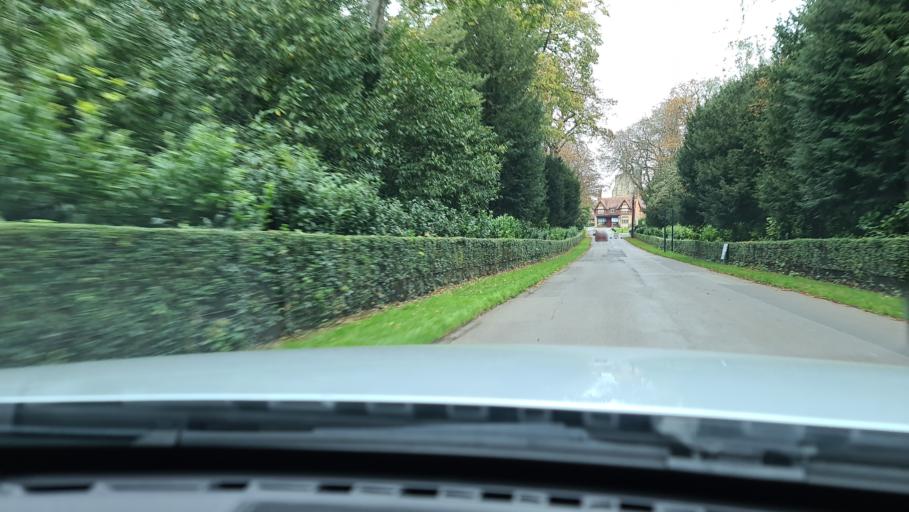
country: GB
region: England
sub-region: Buckinghamshire
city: Waddesdon
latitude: 51.8441
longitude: -0.9248
